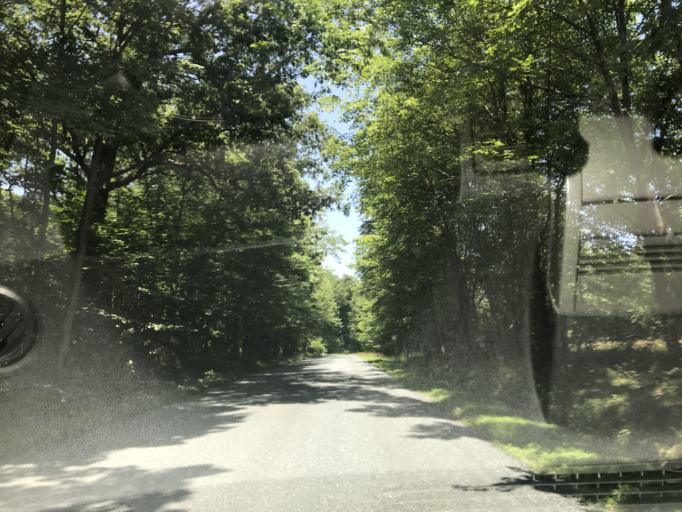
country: US
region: Maryland
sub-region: Harford County
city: Bel Air South
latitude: 39.5454
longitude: -76.2655
